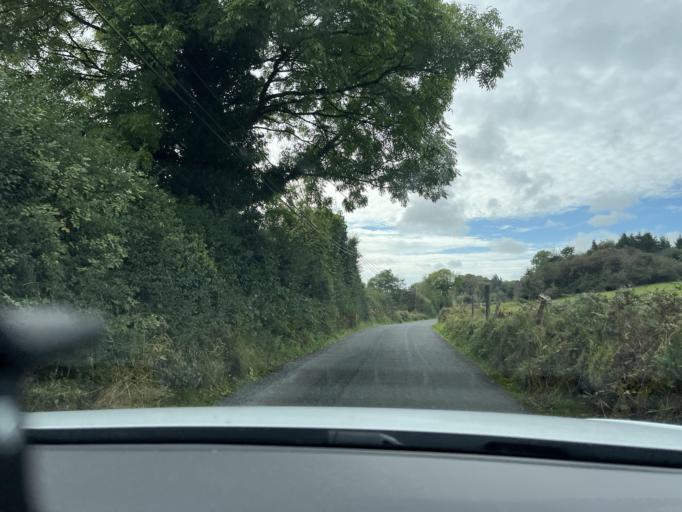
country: IE
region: Connaught
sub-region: Roscommon
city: Boyle
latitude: 54.0209
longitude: -8.3490
